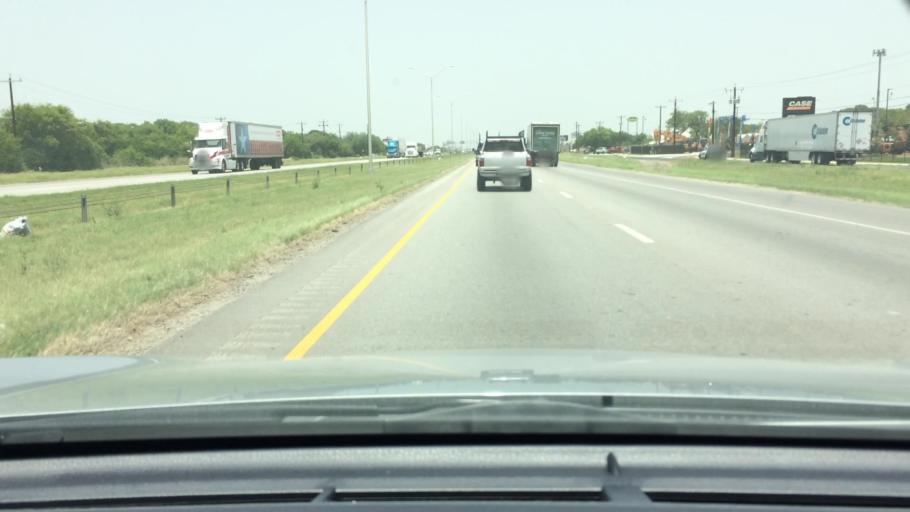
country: US
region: Texas
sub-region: Bexar County
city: China Grove
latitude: 29.4027
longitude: -98.3892
